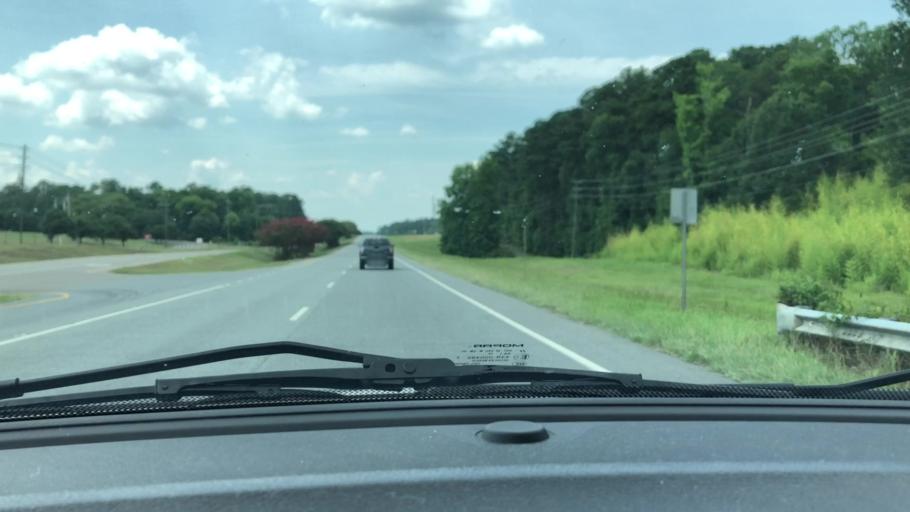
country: US
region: North Carolina
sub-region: Chatham County
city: Farmville
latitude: 35.5177
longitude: -79.2179
